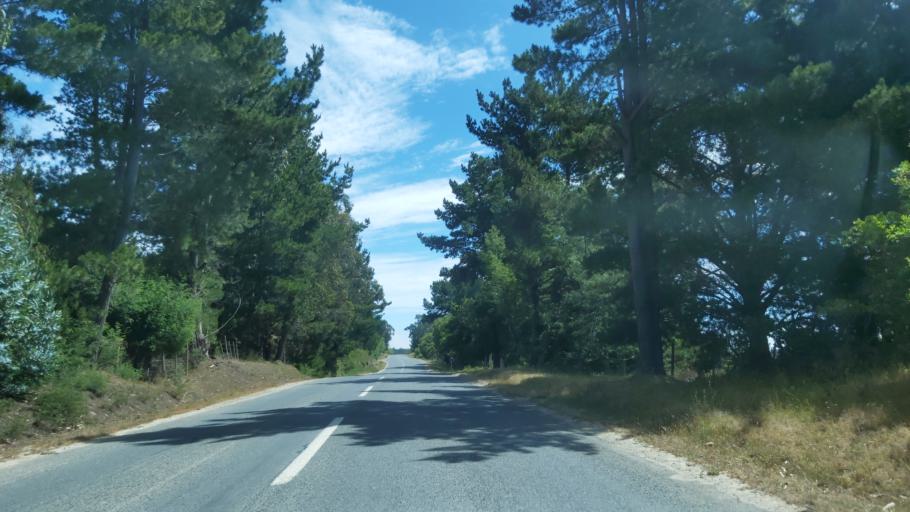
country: CL
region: Maule
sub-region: Provincia de Talca
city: Constitucion
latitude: -35.5617
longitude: -72.5900
